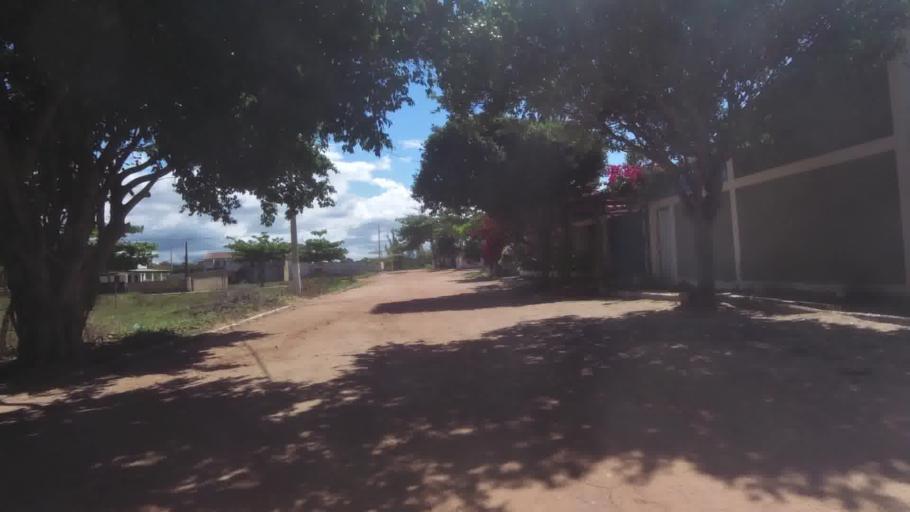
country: BR
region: Espirito Santo
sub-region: Marataizes
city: Marataizes
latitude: -21.2763
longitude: -40.9664
